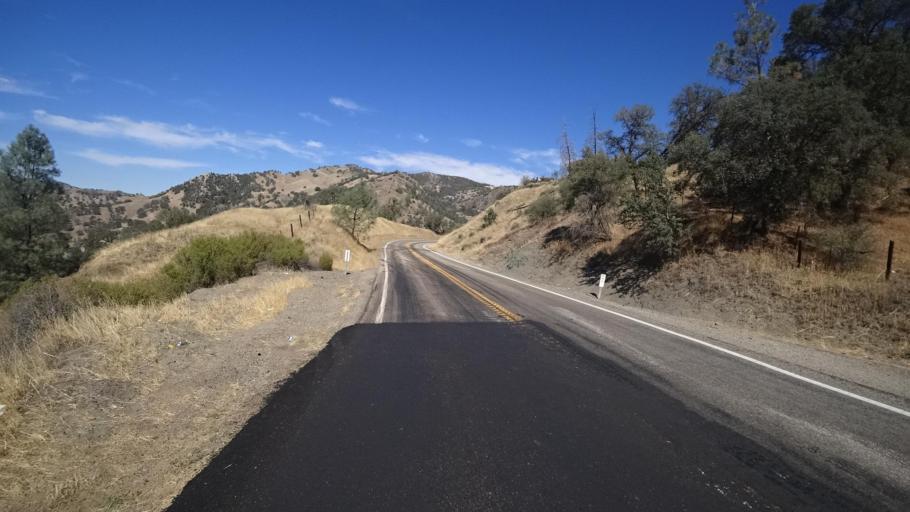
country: US
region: California
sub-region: Fresno County
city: Coalinga
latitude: 36.1975
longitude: -120.7388
